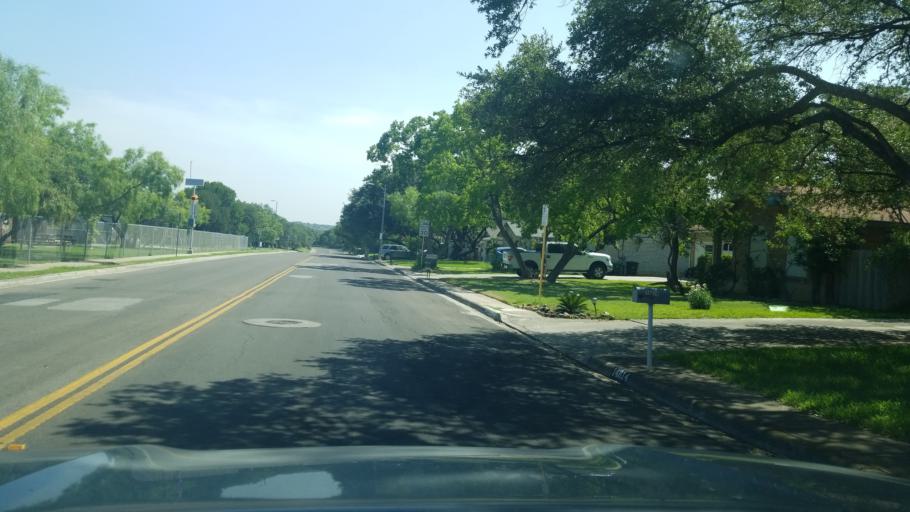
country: US
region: Texas
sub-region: Bexar County
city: Hollywood Park
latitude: 29.5771
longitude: -98.4663
